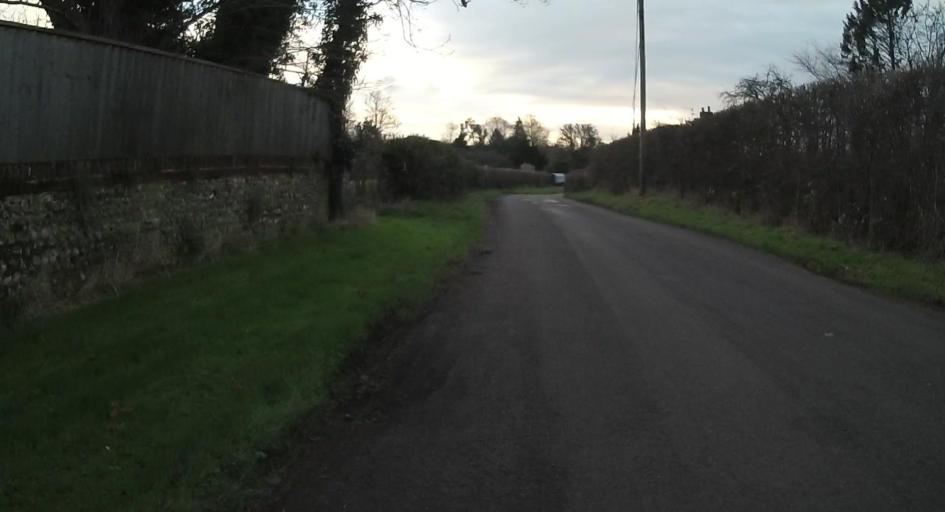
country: GB
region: England
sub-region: Hampshire
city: Swanmore
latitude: 51.0314
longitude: -1.1602
